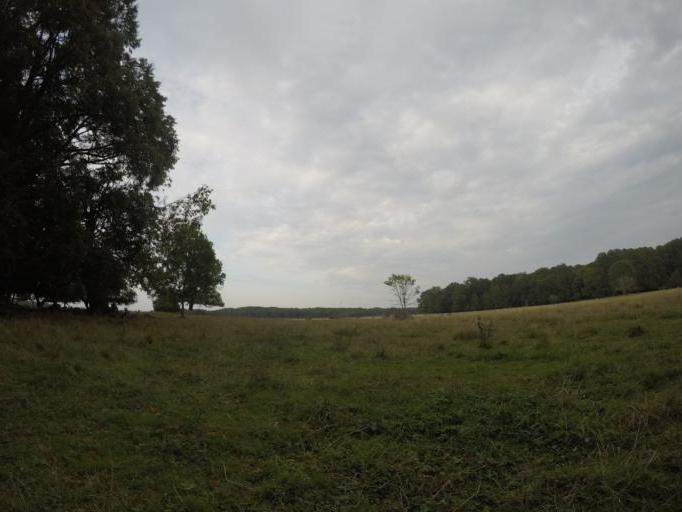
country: SE
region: Vaestmanland
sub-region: Hallstahammars Kommun
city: Kolback
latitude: 59.4702
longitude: 16.2197
